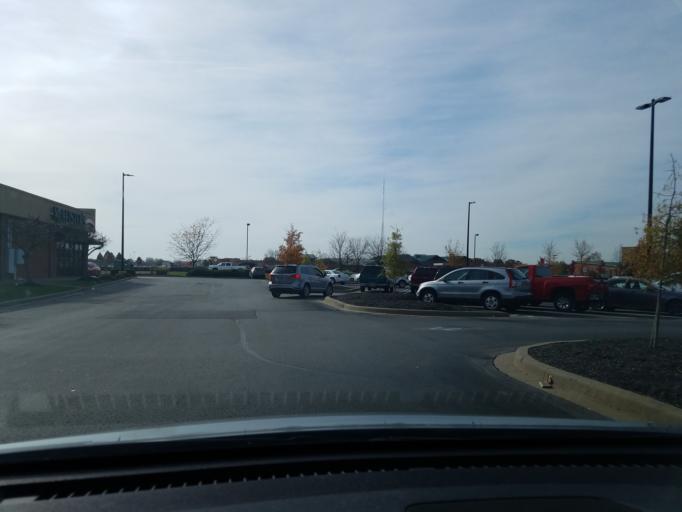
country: US
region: Indiana
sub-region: Clark County
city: Clarksville
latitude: 38.3298
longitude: -85.7598
